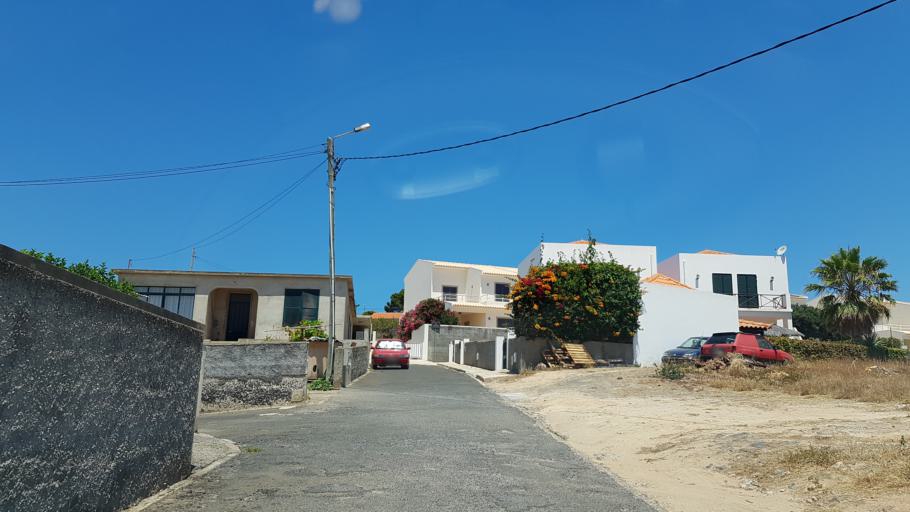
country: PT
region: Madeira
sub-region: Porto Santo
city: Vila de Porto Santo
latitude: 33.0541
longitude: -16.3520
